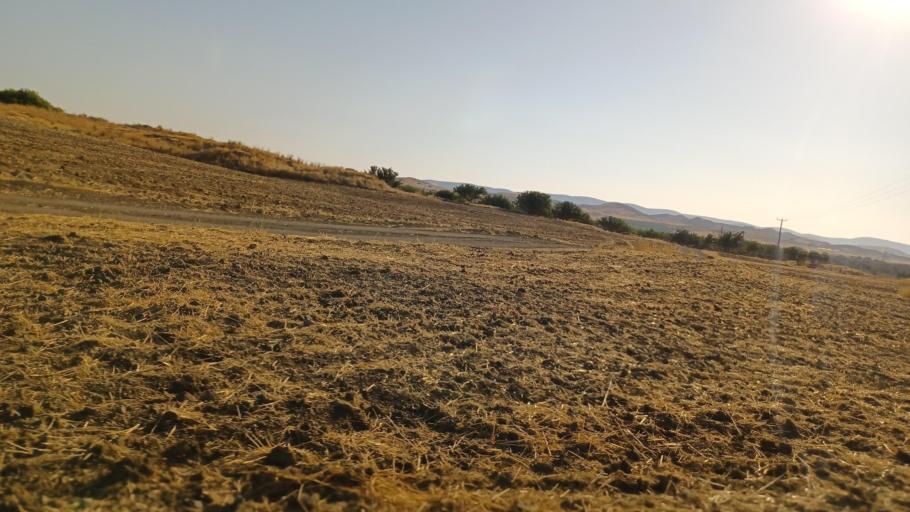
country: CY
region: Larnaka
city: Troulloi
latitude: 35.0151
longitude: 33.5889
